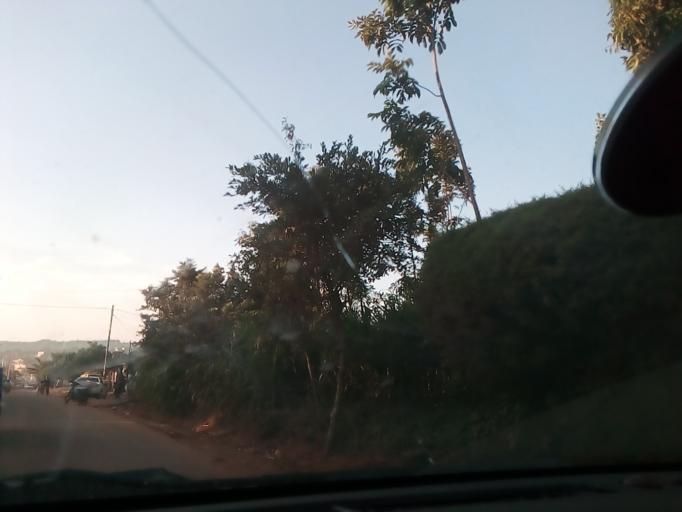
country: UG
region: Central Region
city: Masaka
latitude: -0.3266
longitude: 31.7611
